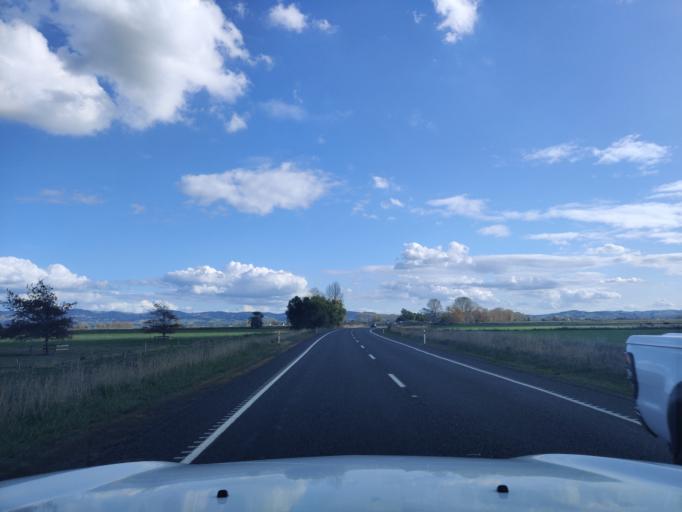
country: NZ
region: Waikato
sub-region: Hauraki District
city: Ngatea
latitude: -37.2777
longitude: 175.4598
